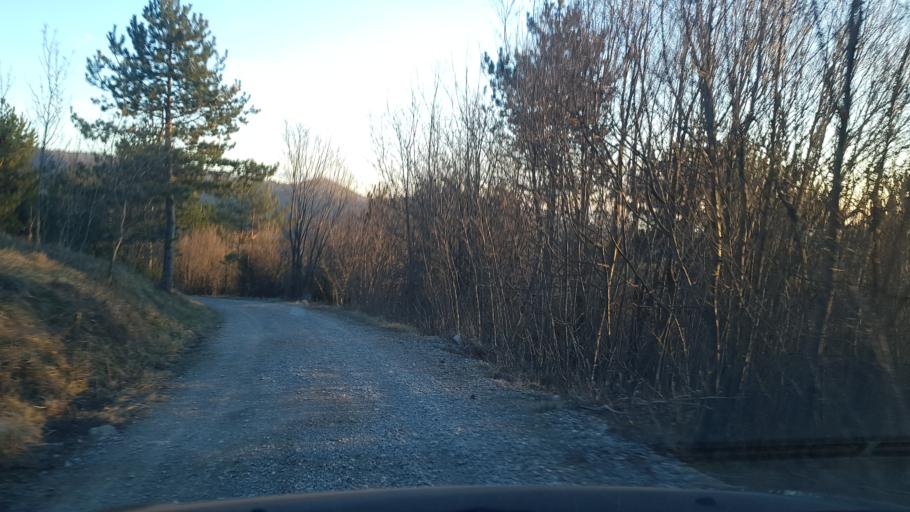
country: SI
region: Nova Gorica
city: Kromberk
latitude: 46.0137
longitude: 13.7034
